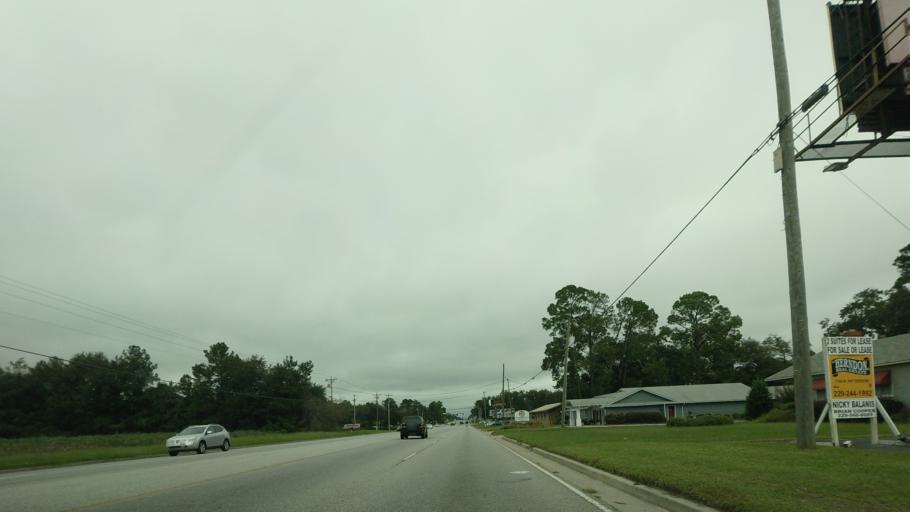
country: US
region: Georgia
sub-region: Lowndes County
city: Valdosta
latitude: 30.8804
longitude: -83.2742
